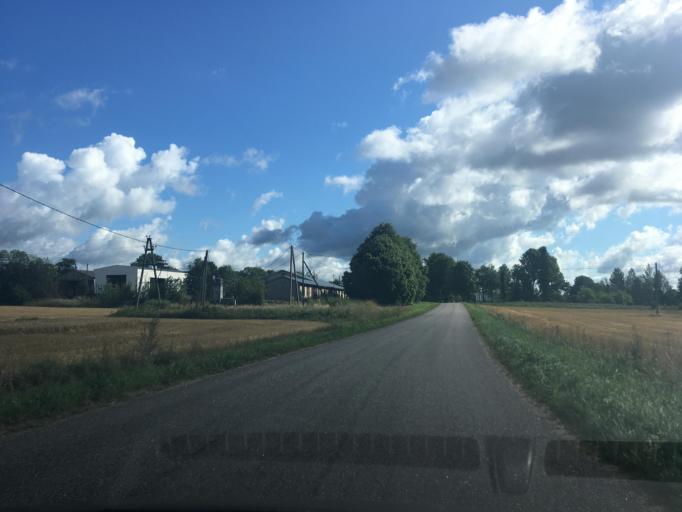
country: EE
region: Jogevamaa
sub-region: Poltsamaa linn
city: Poltsamaa
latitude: 58.4673
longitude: 25.9524
